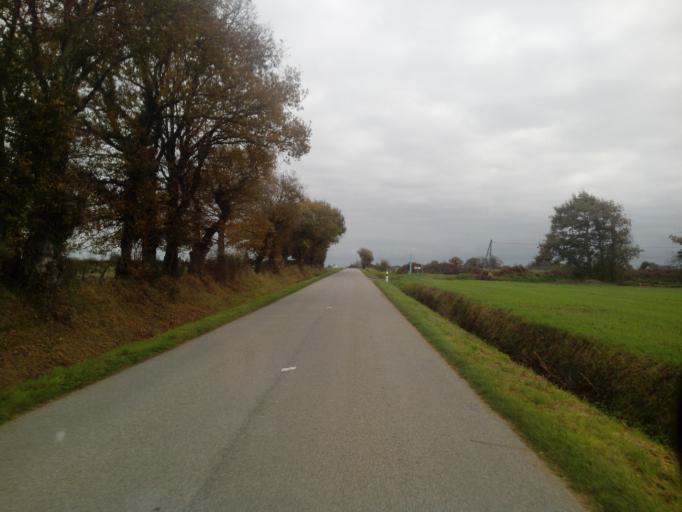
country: FR
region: Brittany
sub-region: Departement du Morbihan
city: Mauron
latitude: 48.0832
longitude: -2.3100
